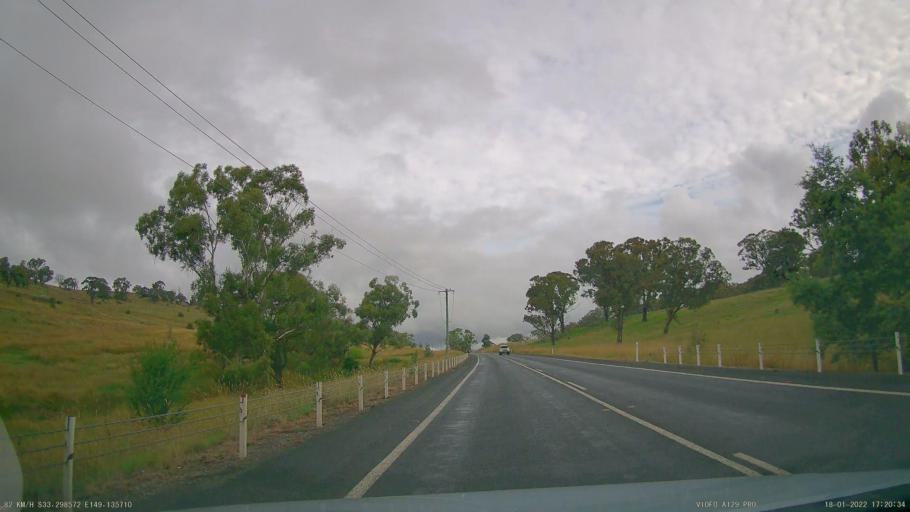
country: AU
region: New South Wales
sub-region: Orange Municipality
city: Orange
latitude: -33.2987
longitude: 149.1357
